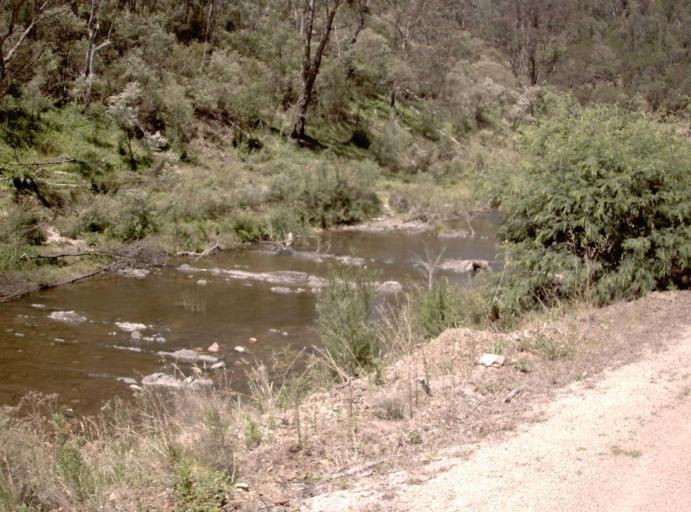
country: AU
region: Victoria
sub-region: East Gippsland
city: Bairnsdale
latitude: -37.4686
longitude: 147.8279
